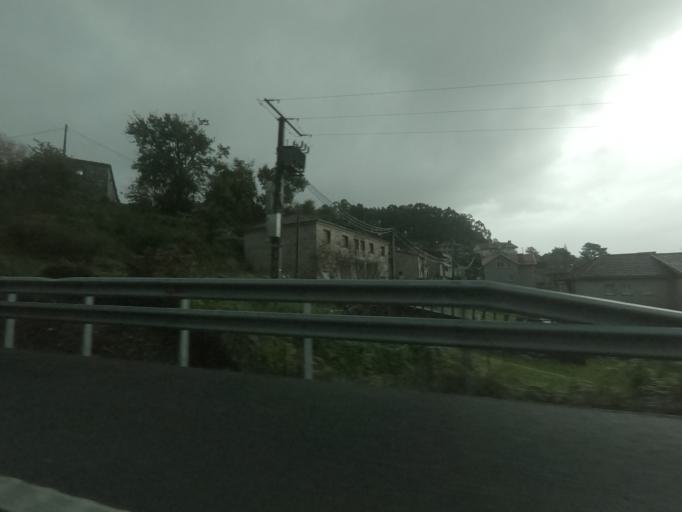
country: ES
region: Galicia
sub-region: Provincia de Pontevedra
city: Redondela
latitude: 42.3306
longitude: -8.6486
